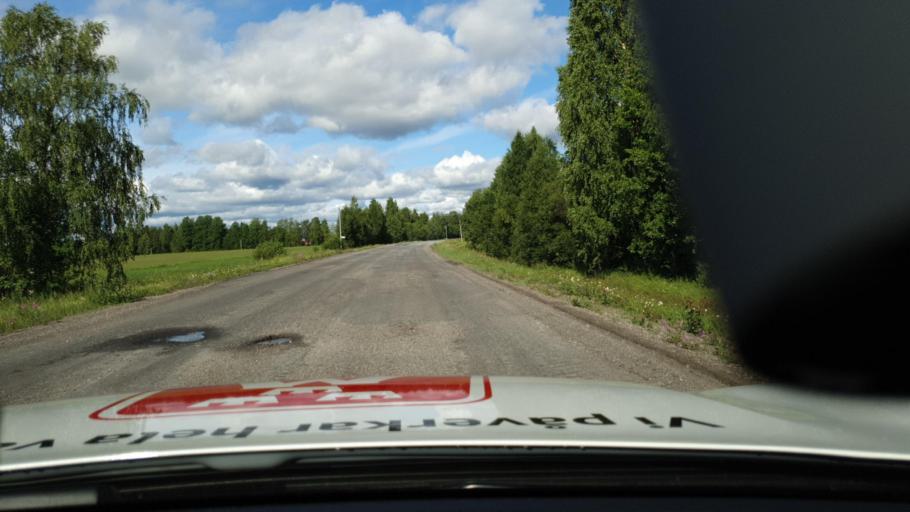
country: SE
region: Norrbotten
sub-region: Bodens Kommun
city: Boden
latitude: 65.8528
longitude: 21.4962
